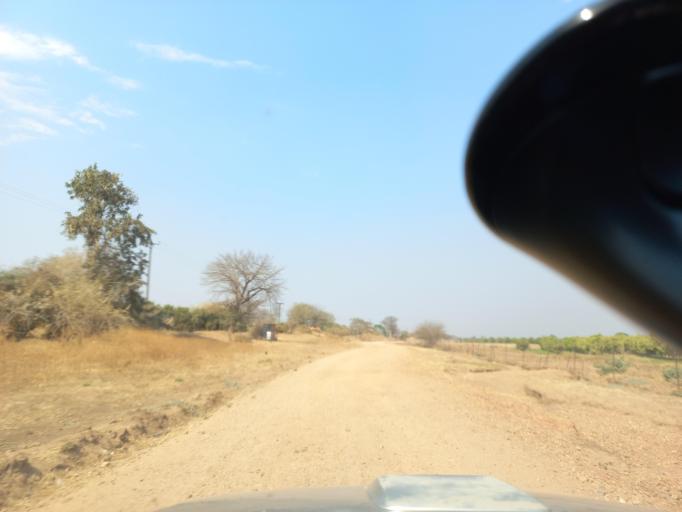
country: ZW
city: Chirundu
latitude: -15.9318
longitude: 28.9517
